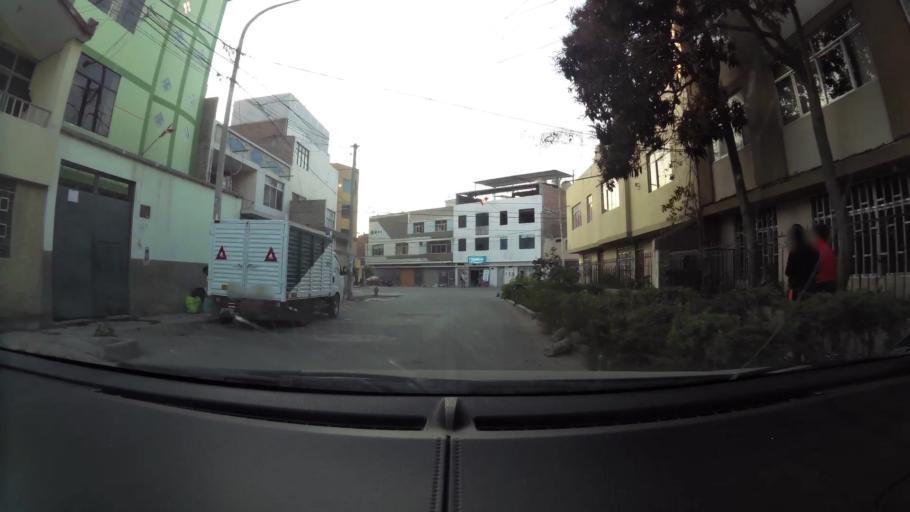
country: PE
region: Lambayeque
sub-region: Provincia de Chiclayo
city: Santa Rosa
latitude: -6.7666
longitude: -79.8340
